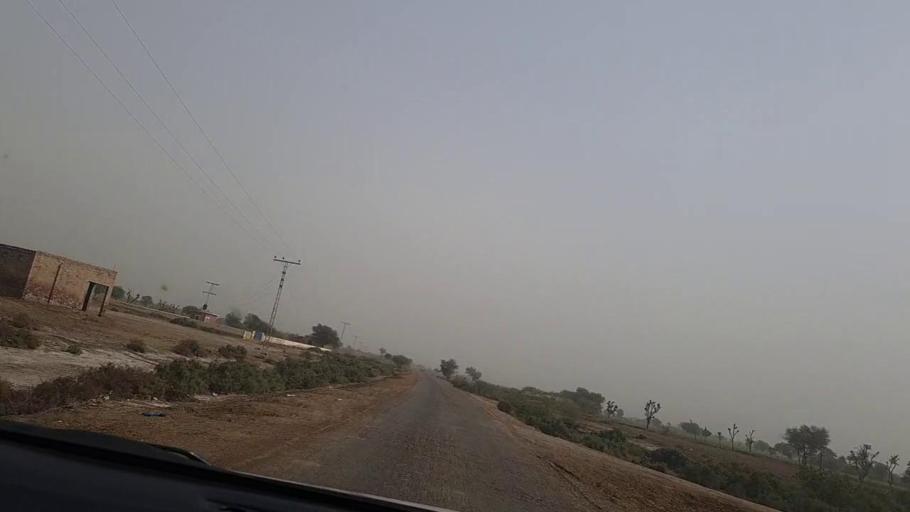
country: PK
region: Sindh
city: Pithoro
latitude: 25.4490
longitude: 69.2887
